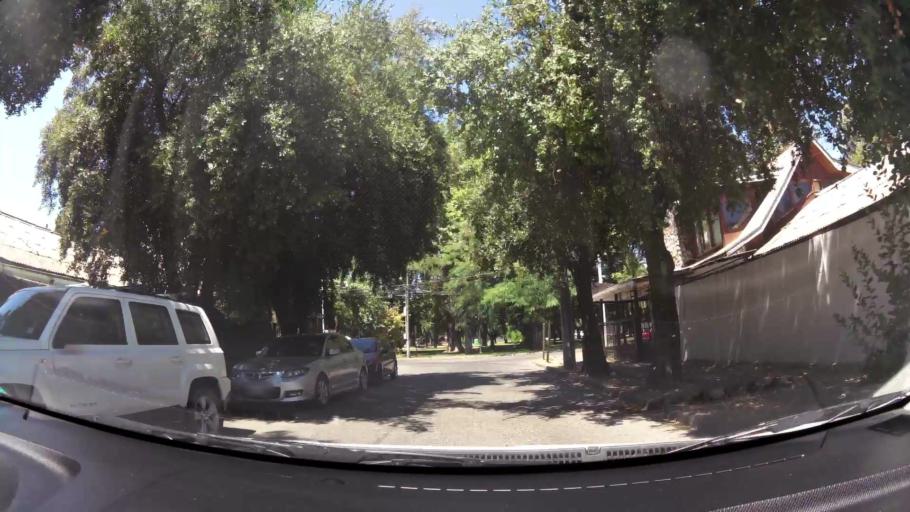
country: CL
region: Maule
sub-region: Provincia de Curico
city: Curico
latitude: -34.9849
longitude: -71.2303
